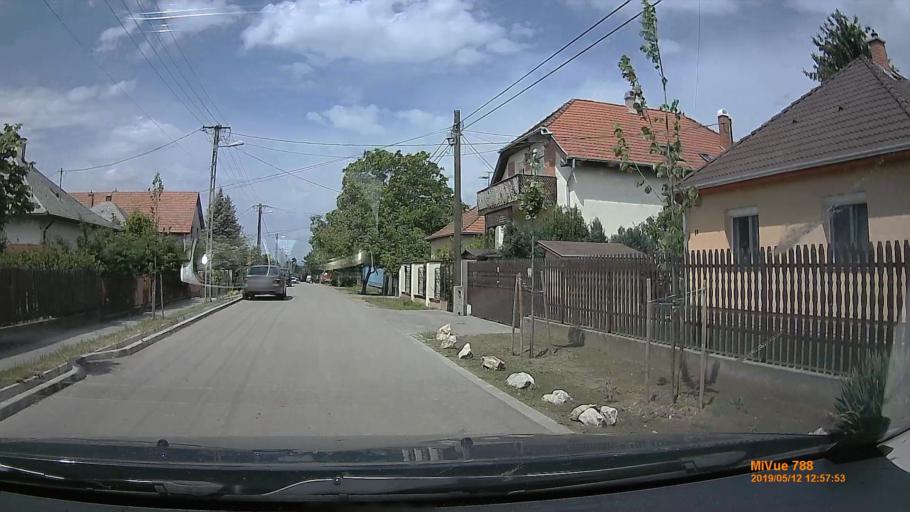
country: HU
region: Pest
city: Ecser
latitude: 47.4745
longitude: 19.2975
